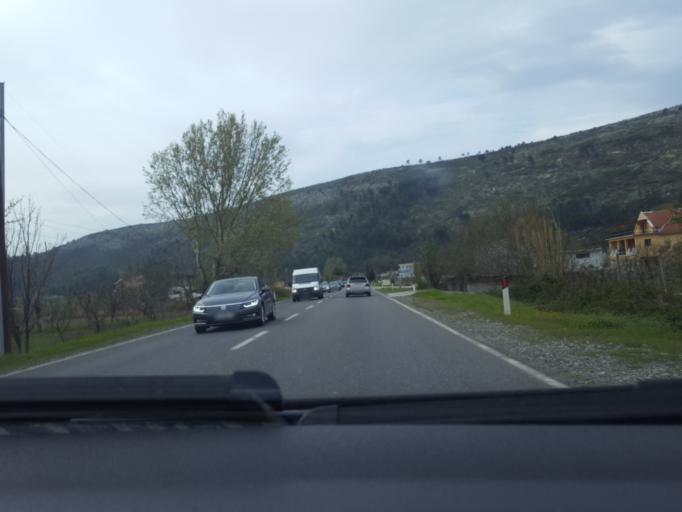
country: AL
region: Lezhe
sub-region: Rrethi i Lezhes
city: Balldreni i Ri
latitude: 41.8068
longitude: 19.6330
